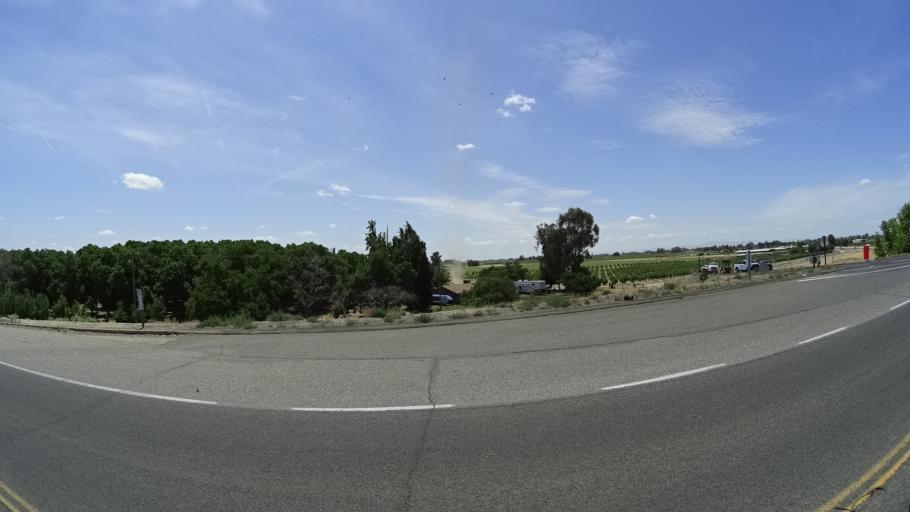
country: US
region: California
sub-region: Kings County
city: Lemoore
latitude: 36.2972
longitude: -119.7537
